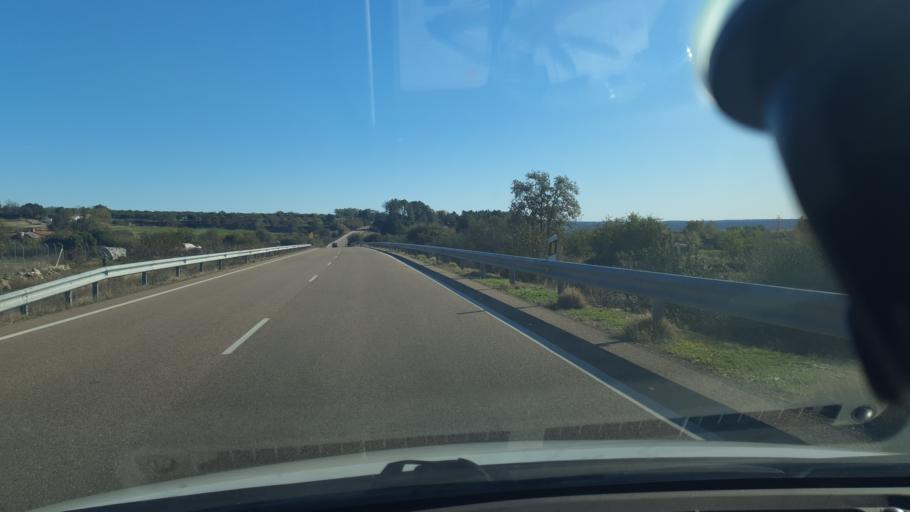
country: ES
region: Castille and Leon
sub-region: Provincia de Avila
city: Candeleda
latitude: 40.1377
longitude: -5.2449
